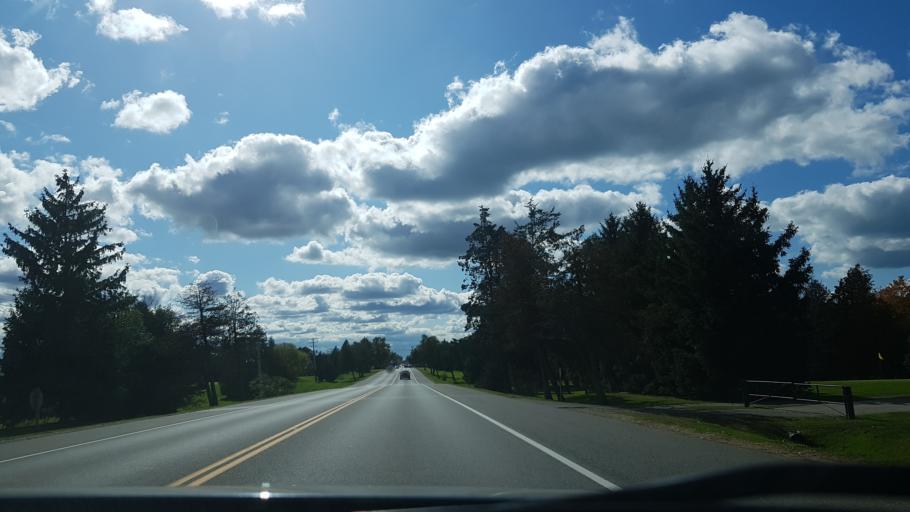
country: CA
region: Ontario
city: Bluewater
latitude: 43.3209
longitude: -81.7499
